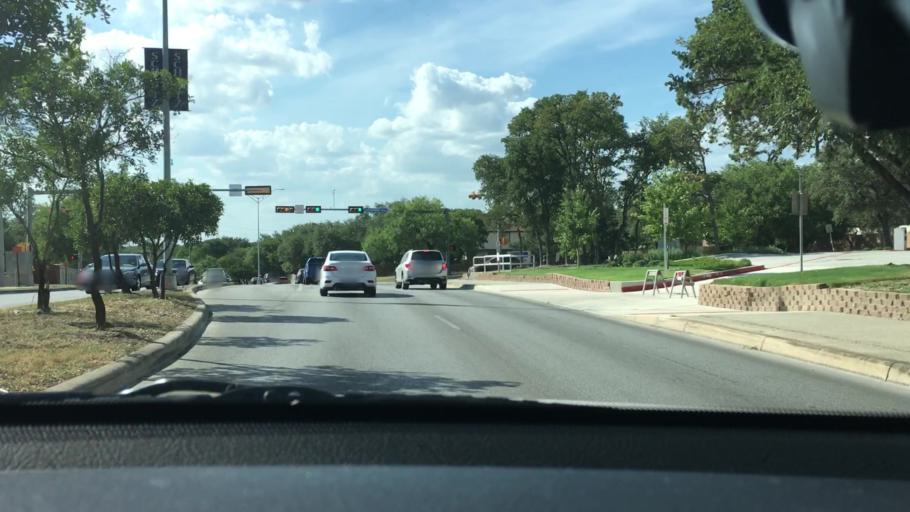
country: US
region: Texas
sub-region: Bexar County
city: Selma
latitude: 29.5815
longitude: -98.2819
